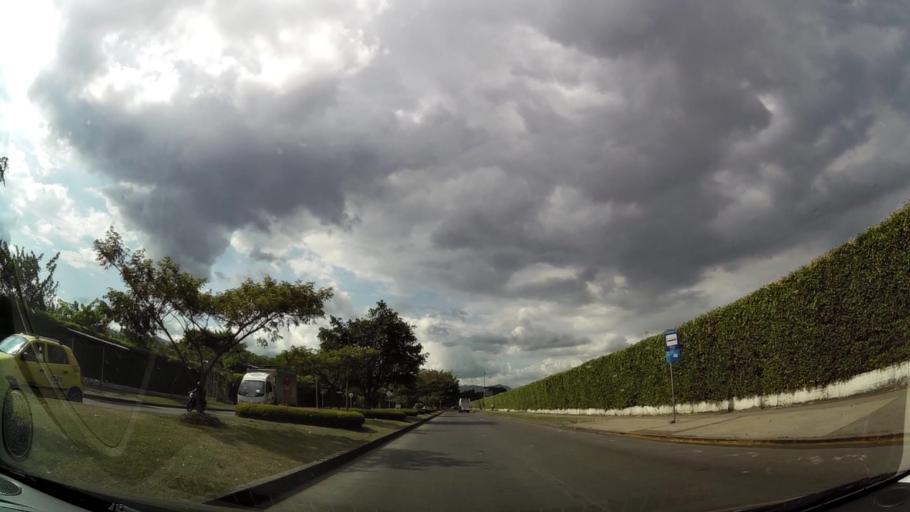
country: CO
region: Valle del Cauca
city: Cali
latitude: 3.4544
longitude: -76.5055
